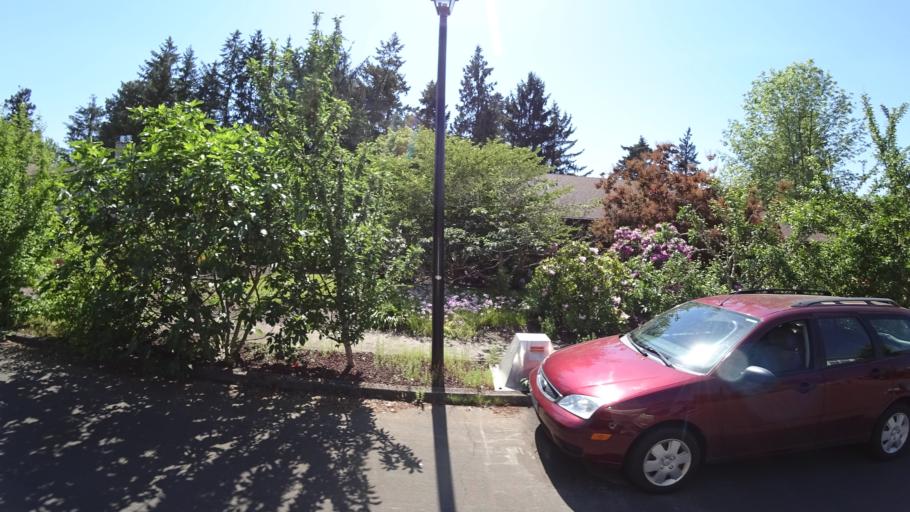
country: US
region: Oregon
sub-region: Washington County
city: Rockcreek
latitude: 45.5485
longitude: -122.8771
